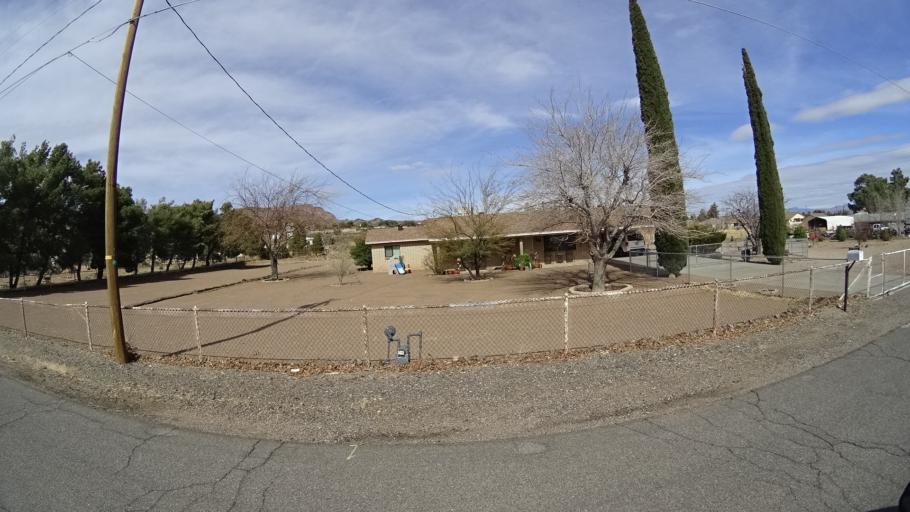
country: US
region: Arizona
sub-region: Mohave County
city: New Kingman-Butler
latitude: 35.2305
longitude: -114.0518
